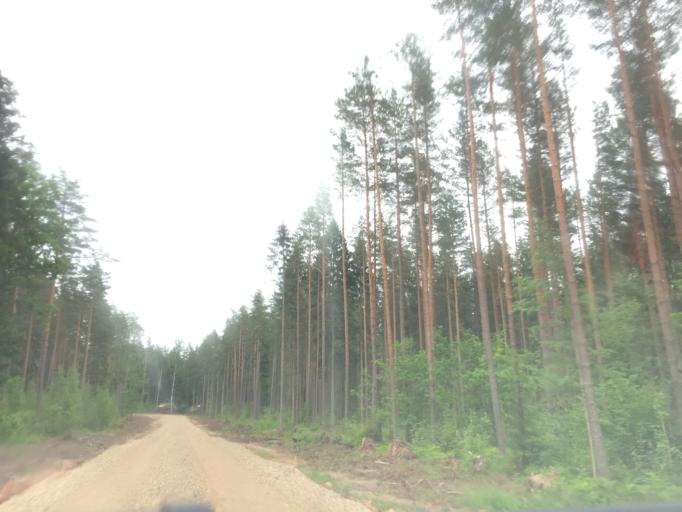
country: LV
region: Tukuma Rajons
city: Tukums
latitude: 57.0042
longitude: 23.1079
